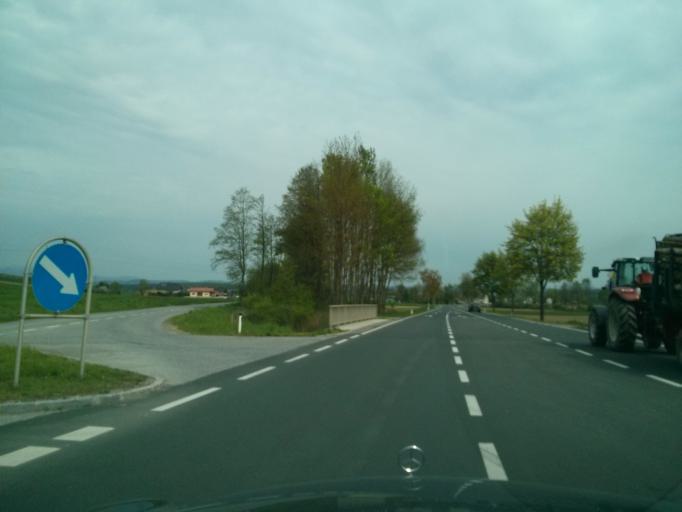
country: AT
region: Burgenland
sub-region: Politischer Bezirk Oberwart
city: Oberwart
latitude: 47.3089
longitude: 16.2066
